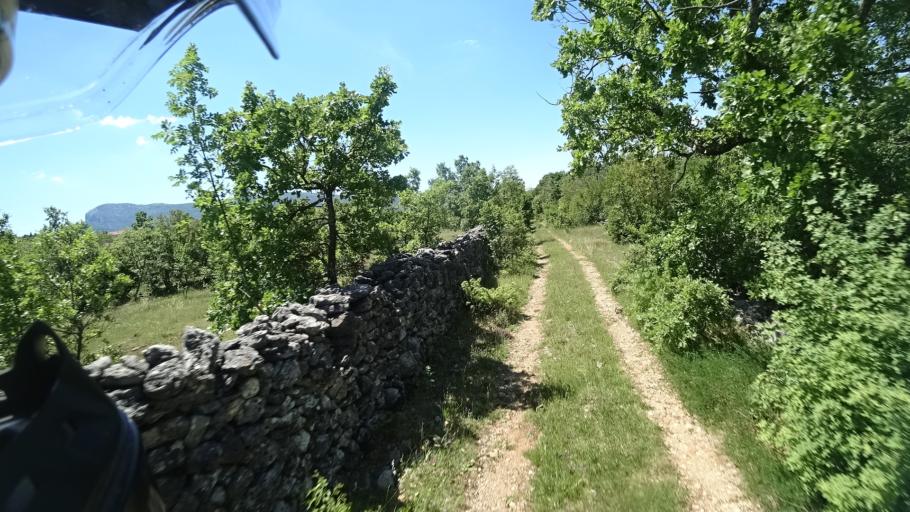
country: HR
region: Sibensko-Kniniska
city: Knin
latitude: 44.0066
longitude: 16.3114
